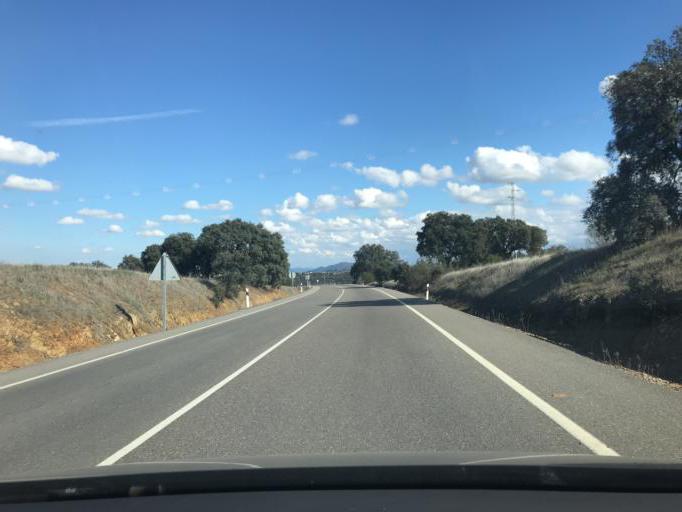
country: ES
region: Andalusia
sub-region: Province of Cordoba
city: Fuente Obejuna
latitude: 38.2590
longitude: -5.4729
